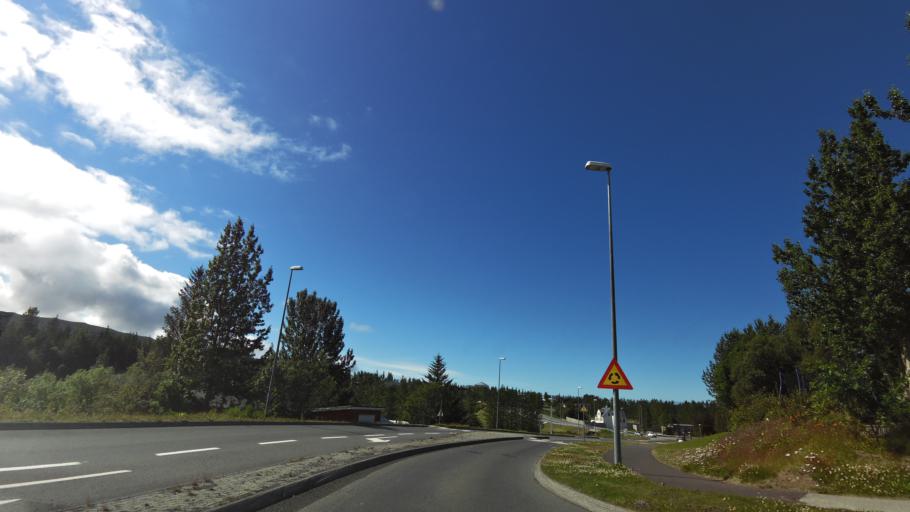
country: IS
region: Capital Region
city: Mosfellsbaer
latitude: 64.1672
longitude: -21.6802
